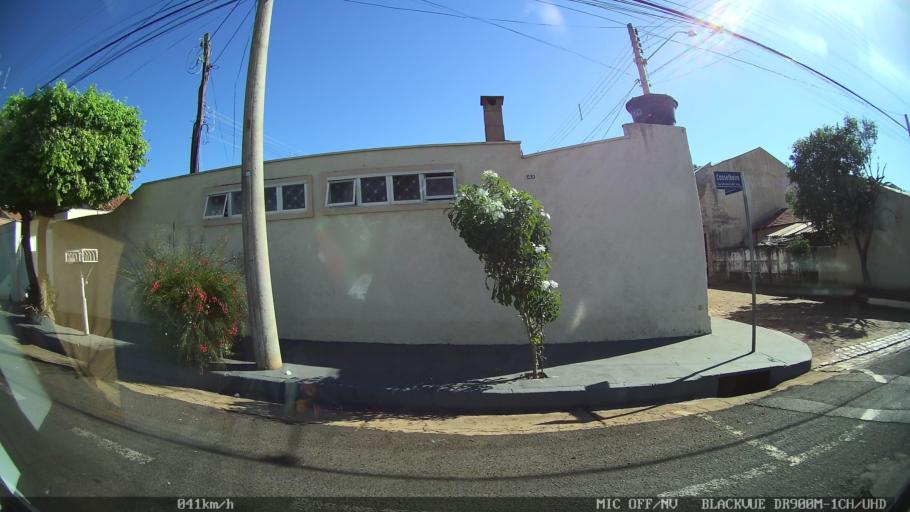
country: BR
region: Sao Paulo
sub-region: Olimpia
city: Olimpia
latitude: -20.7485
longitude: -48.9140
